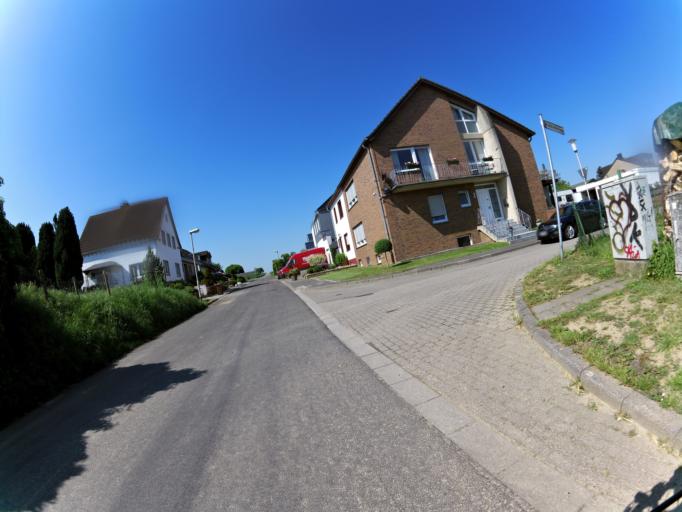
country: DE
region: North Rhine-Westphalia
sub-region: Regierungsbezirk Koln
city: Linnich
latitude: 51.0020
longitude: 6.2414
